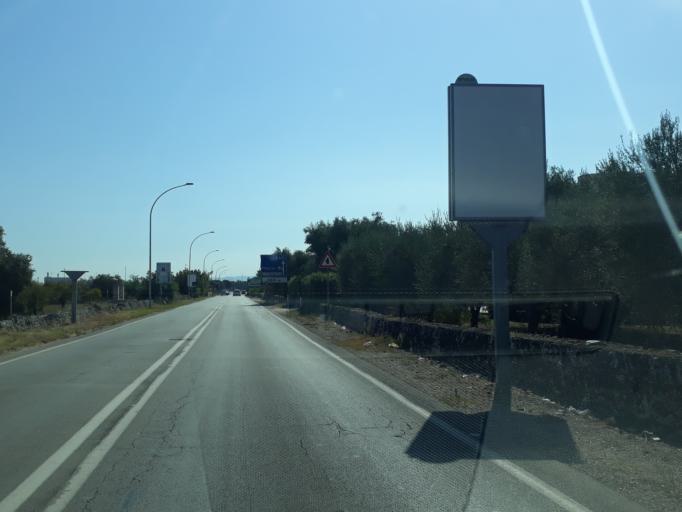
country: IT
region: Apulia
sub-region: Provincia di Bari
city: Monopoli
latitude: 40.9291
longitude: 17.3127
